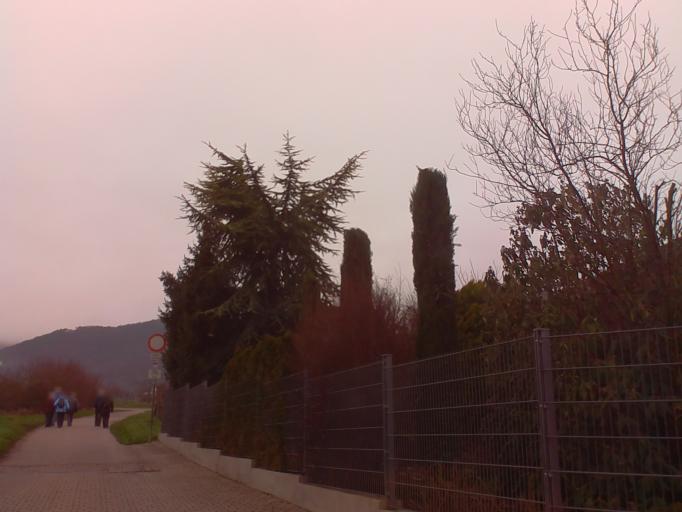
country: DE
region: Rheinland-Pfalz
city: Maikammer
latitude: 49.3212
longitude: 8.1318
